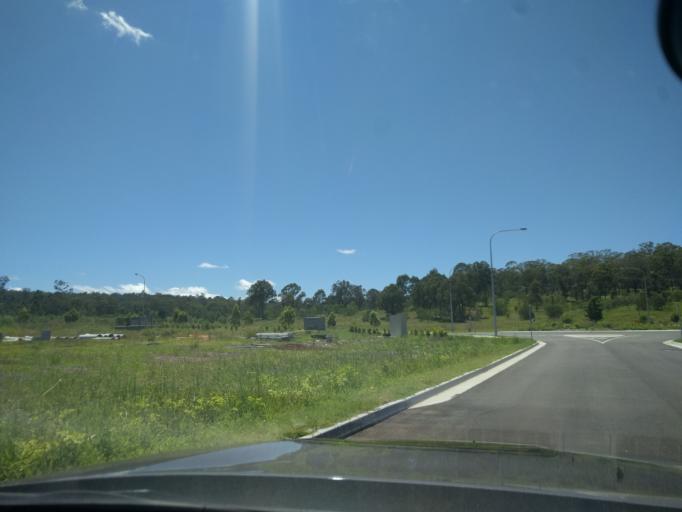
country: AU
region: Queensland
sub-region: Logan
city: Cedar Vale
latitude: -27.9925
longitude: 153.0111
